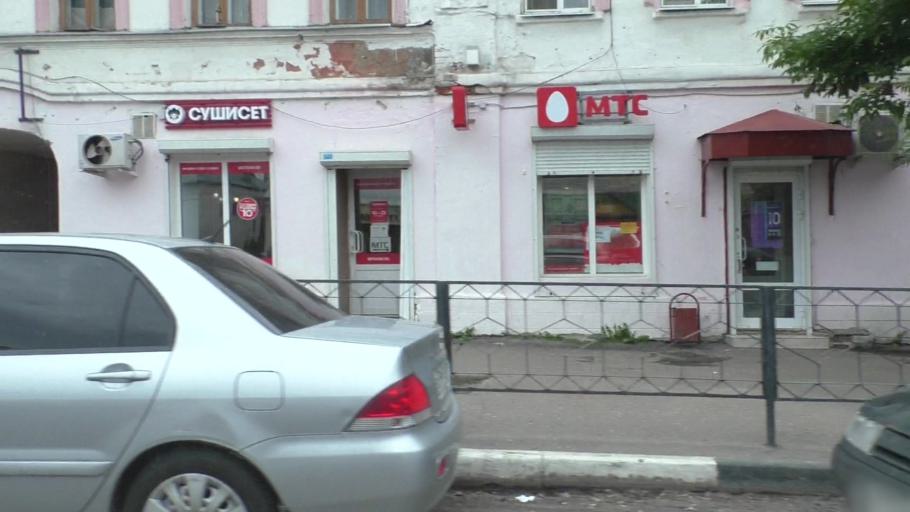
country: RU
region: Moskovskaya
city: Yegor'yevsk
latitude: 55.3799
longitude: 39.0406
